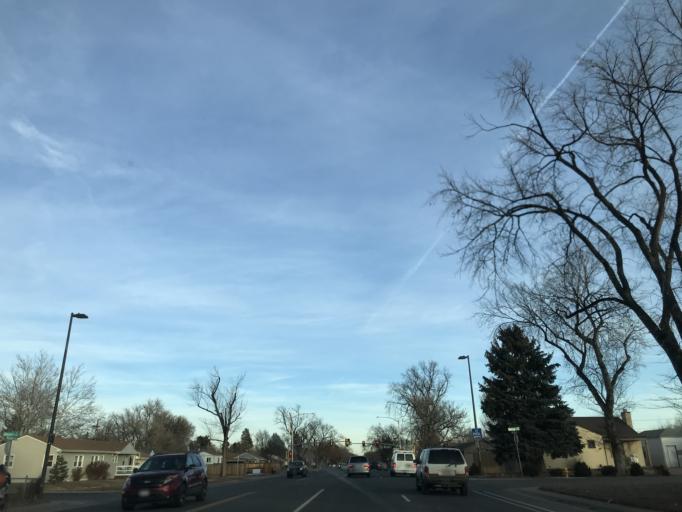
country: US
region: Colorado
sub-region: Adams County
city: Aurora
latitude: 39.7474
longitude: -104.8675
